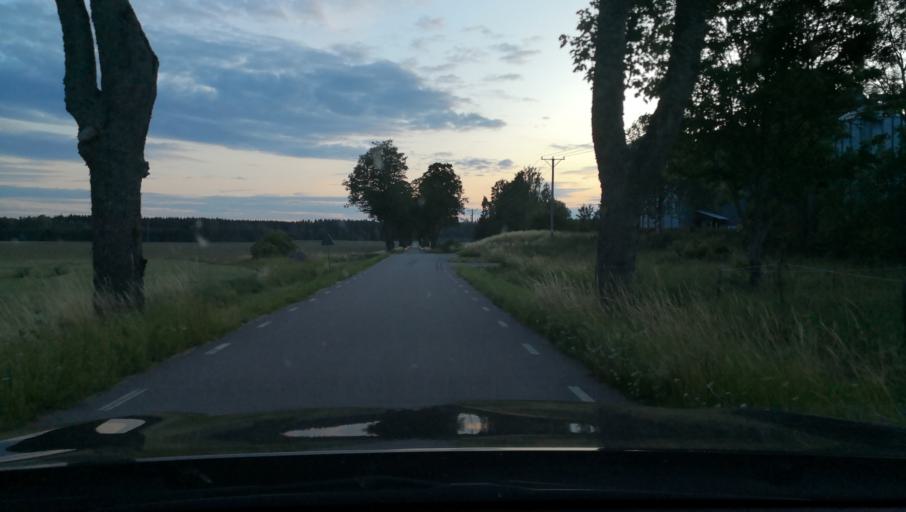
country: SE
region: Uppsala
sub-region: Osthammars Kommun
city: Bjorklinge
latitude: 60.0616
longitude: 17.5629
